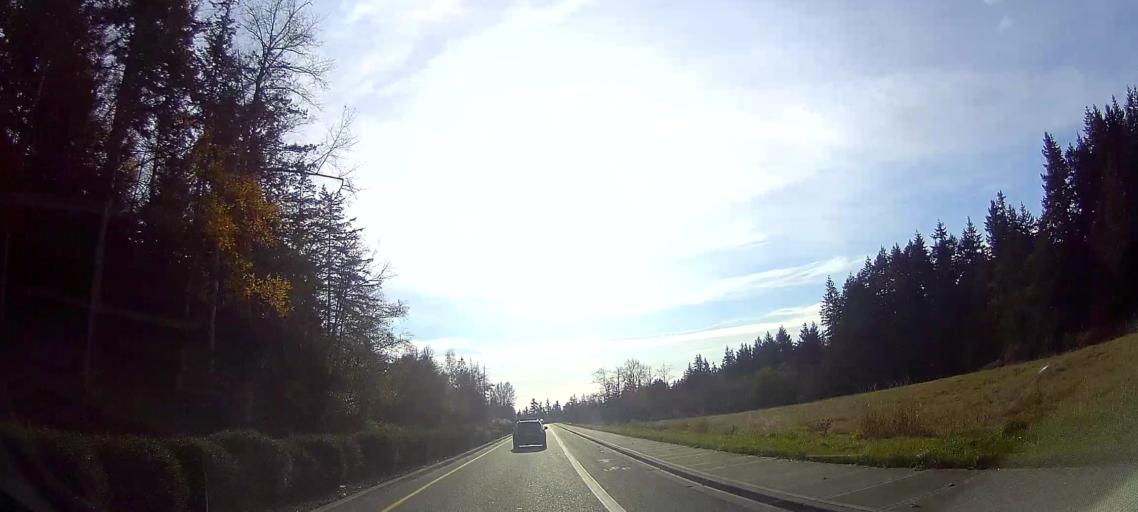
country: US
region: Washington
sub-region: Skagit County
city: Mount Vernon
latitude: 48.4037
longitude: -122.3143
